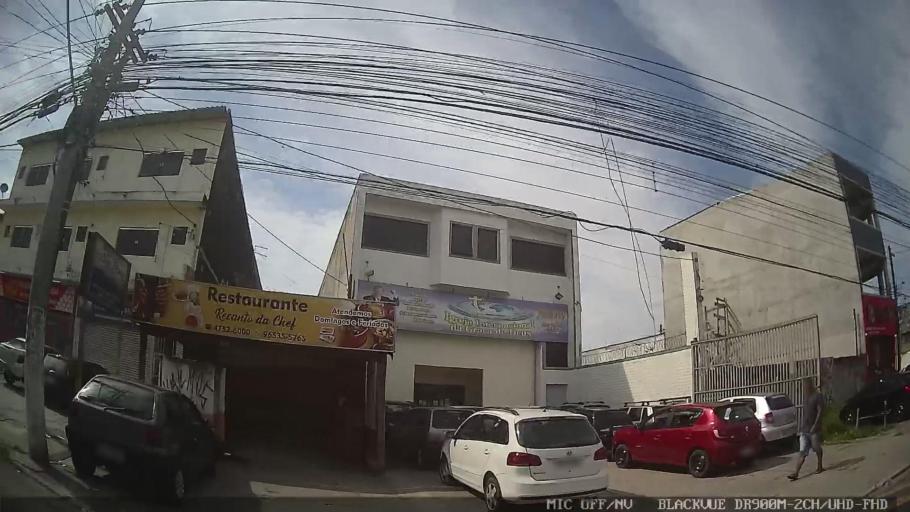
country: BR
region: Sao Paulo
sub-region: Itaquaquecetuba
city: Itaquaquecetuba
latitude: -23.4941
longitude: -46.3188
